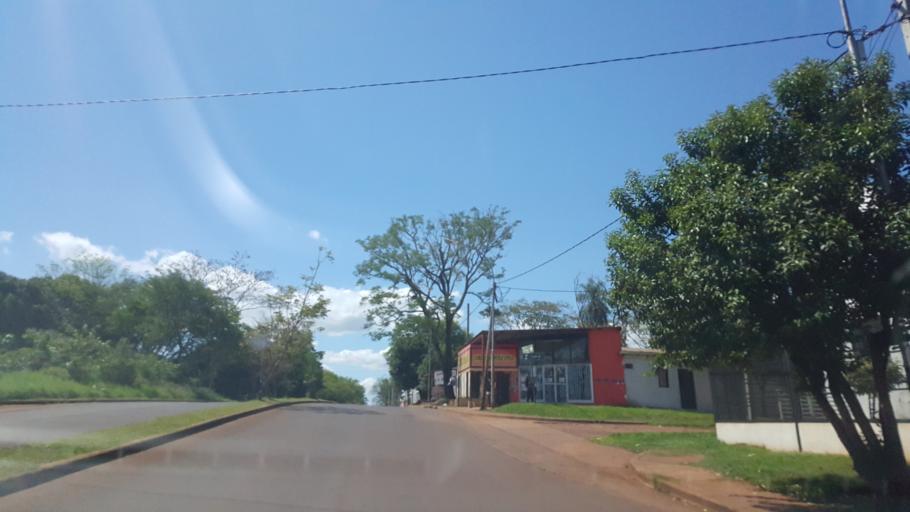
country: AR
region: Misiones
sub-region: Departamento de Capital
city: Posadas
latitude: -27.3618
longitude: -55.9385
